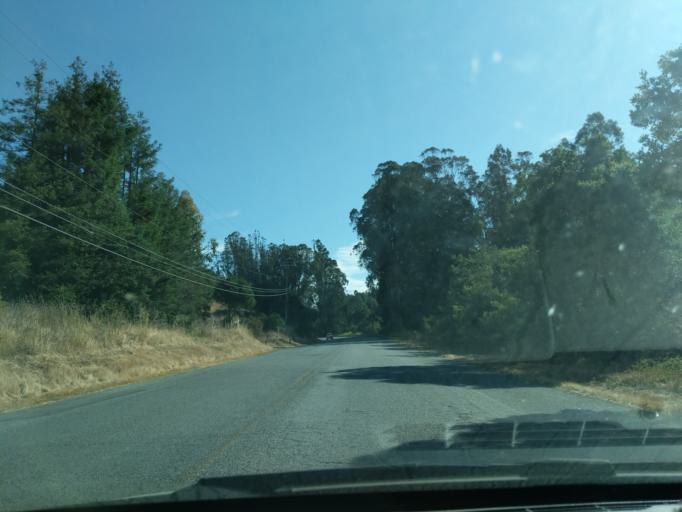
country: US
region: California
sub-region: San Benito County
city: Aromas
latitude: 36.8650
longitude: -121.6483
